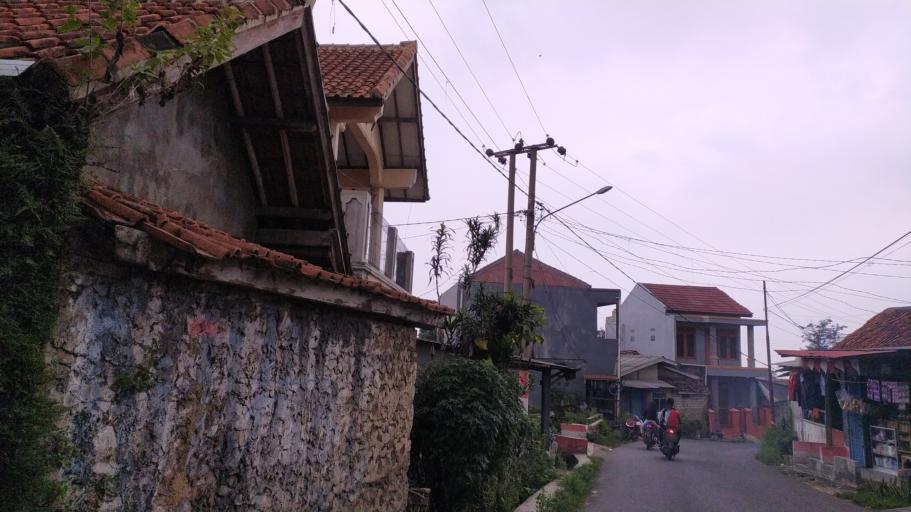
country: ID
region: West Java
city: Ciampea
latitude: -6.6136
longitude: 106.6953
